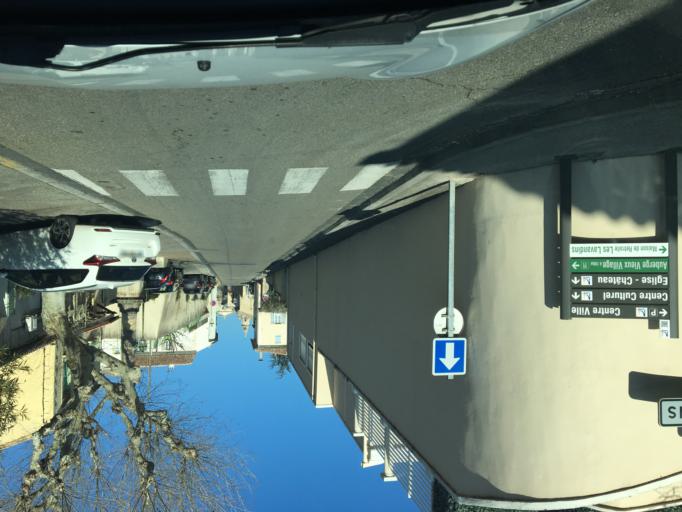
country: FR
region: Provence-Alpes-Cote d'Azur
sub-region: Departement des Bouches-du-Rhone
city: Mallemort
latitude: 43.7293
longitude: 5.1809
